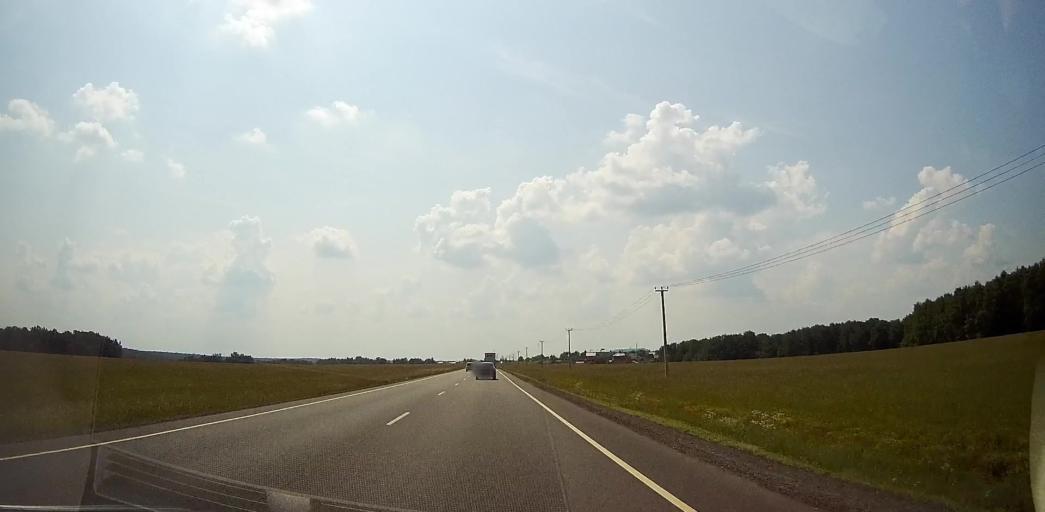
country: RU
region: Moskovskaya
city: Meshcherino
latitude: 55.1529
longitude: 38.3034
